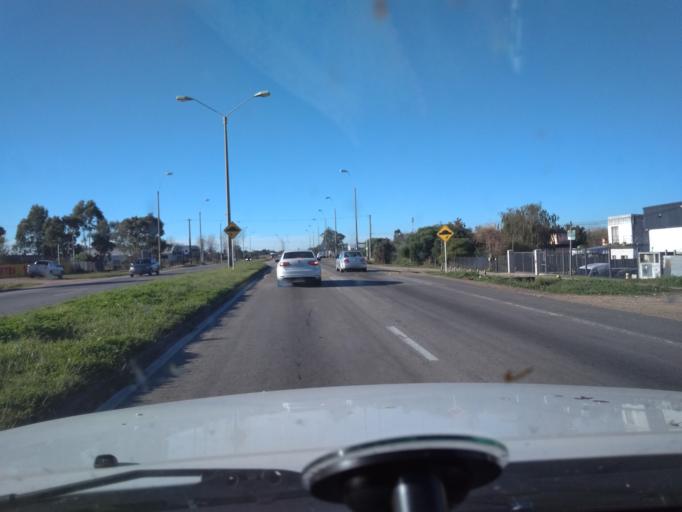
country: UY
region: Canelones
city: Colonia Nicolich
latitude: -34.7794
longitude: -56.0574
